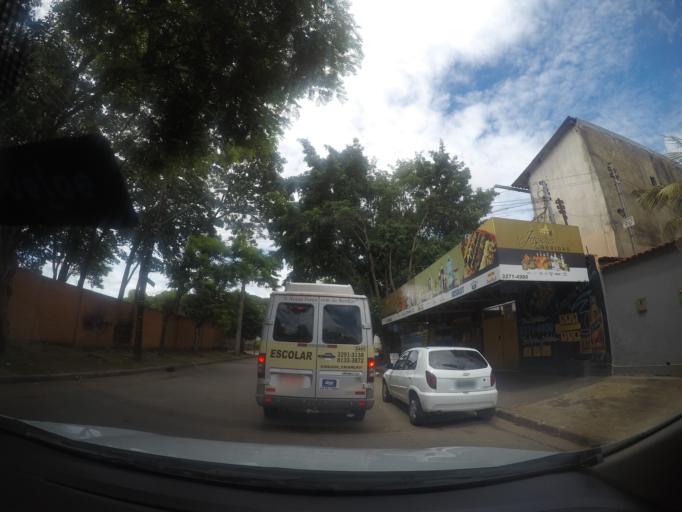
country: BR
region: Goias
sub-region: Goiania
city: Goiania
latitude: -16.6613
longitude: -49.2981
